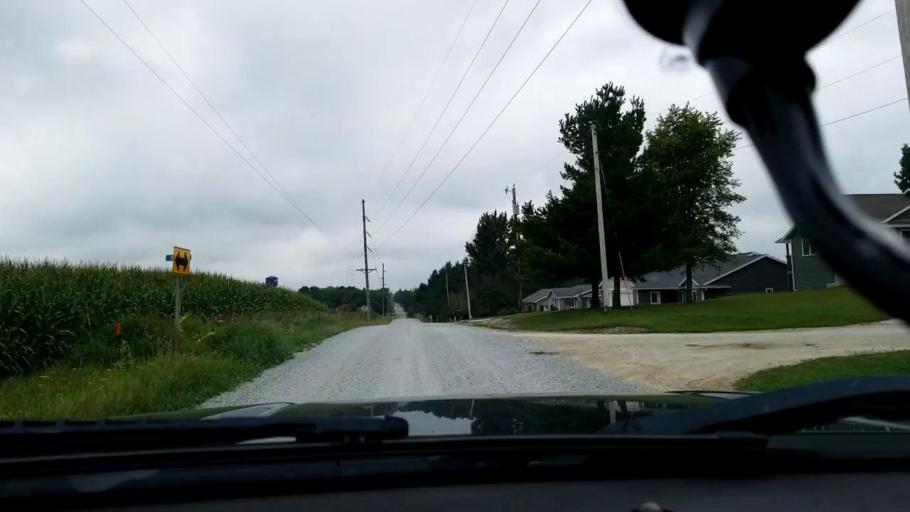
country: US
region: Iowa
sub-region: Buchanan County
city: Independence
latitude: 42.4887
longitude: -91.8845
